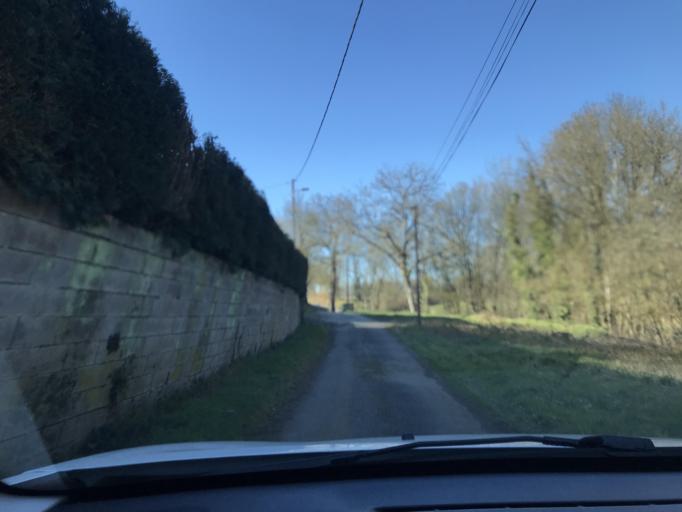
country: FR
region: Poitou-Charentes
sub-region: Departement de la Charente
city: Saint-Claud
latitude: 45.8469
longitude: 0.5066
